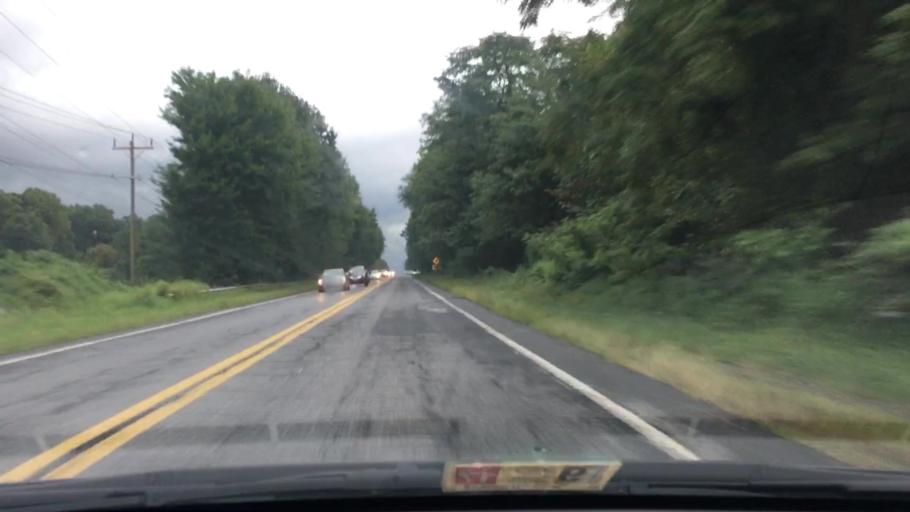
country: US
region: Maryland
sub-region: Montgomery County
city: Redland
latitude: 39.1859
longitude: -77.1334
